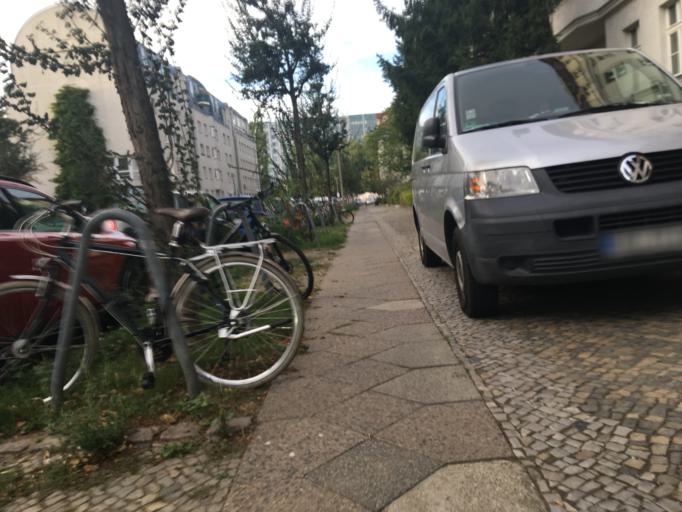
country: DE
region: Berlin
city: Lichtenberg
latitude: 52.5171
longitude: 13.4970
